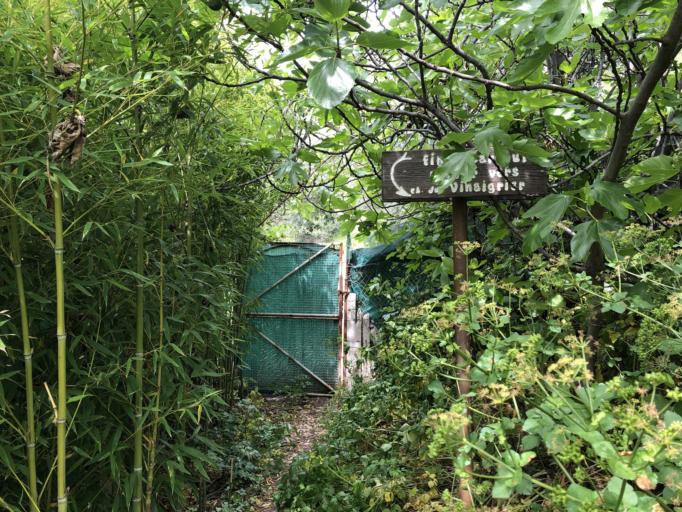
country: FR
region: Provence-Alpes-Cote d'Azur
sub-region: Departement des Alpes-Maritimes
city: Saint-Andre-de-la-Roche
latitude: 43.7237
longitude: 7.2970
